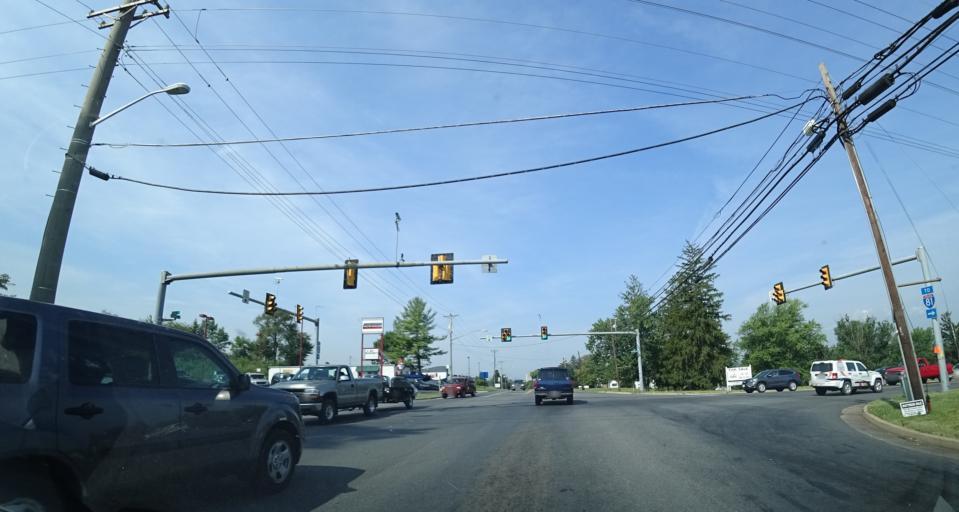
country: US
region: Virginia
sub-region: City of Harrisonburg
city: Harrisonburg
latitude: 38.4632
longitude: -78.8498
